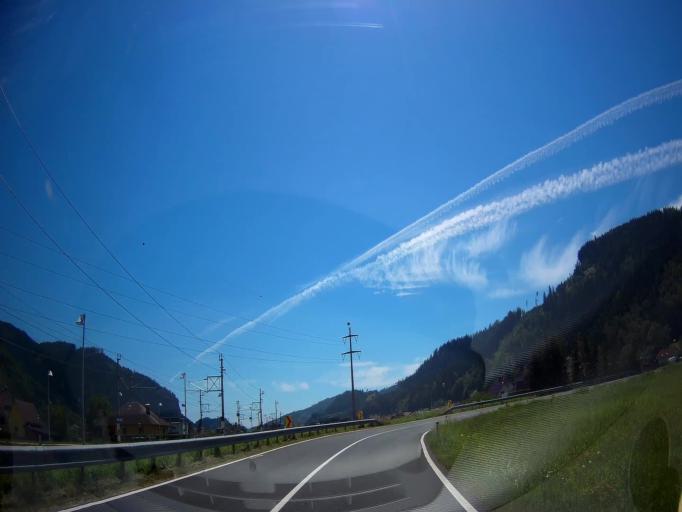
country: AT
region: Carinthia
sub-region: Politischer Bezirk Sankt Veit an der Glan
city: Micheldorf
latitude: 46.9152
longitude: 14.4311
